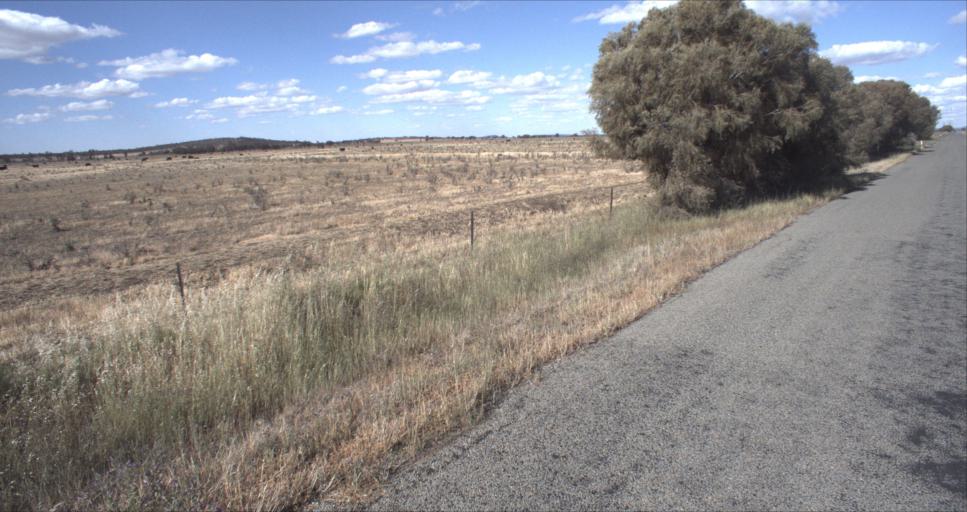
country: AU
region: New South Wales
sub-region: Leeton
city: Leeton
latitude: -34.4409
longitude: 146.2293
